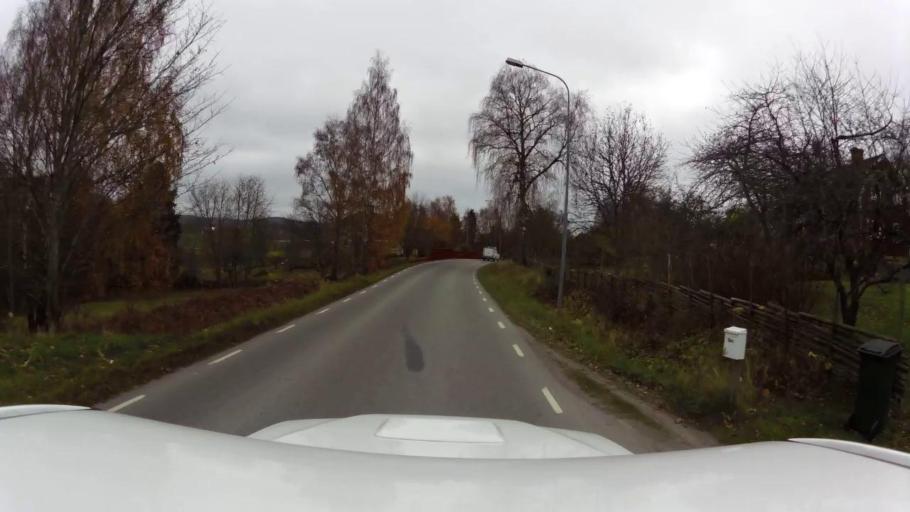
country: SE
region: OEstergoetland
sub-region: Kinda Kommun
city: Rimforsa
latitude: 58.1418
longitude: 15.6730
